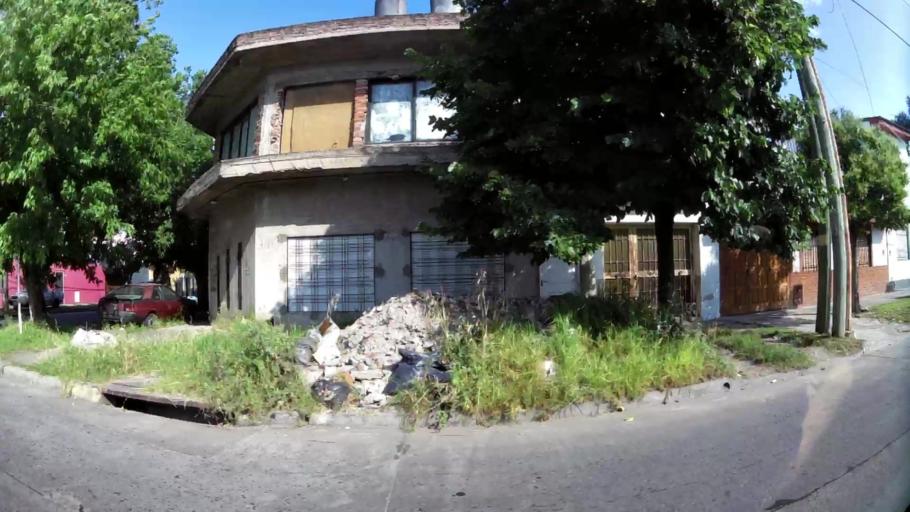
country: AR
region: Buenos Aires
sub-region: Partido de Moron
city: Moron
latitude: -34.6609
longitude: -58.5925
